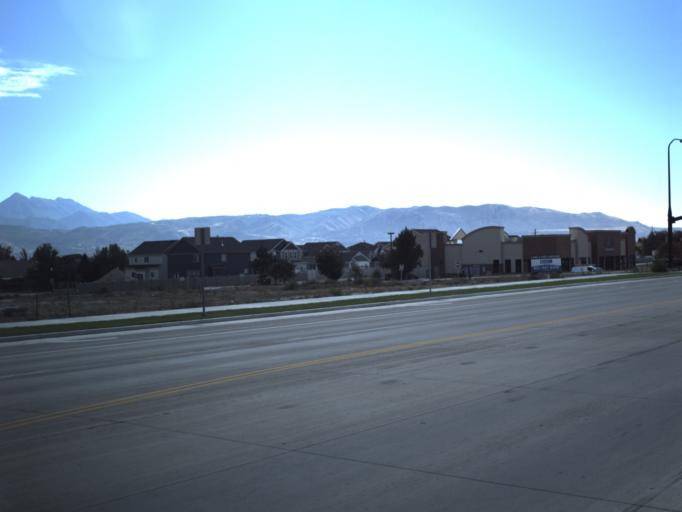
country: US
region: Utah
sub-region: Salt Lake County
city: South Jordan
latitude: 40.5521
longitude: -111.9388
